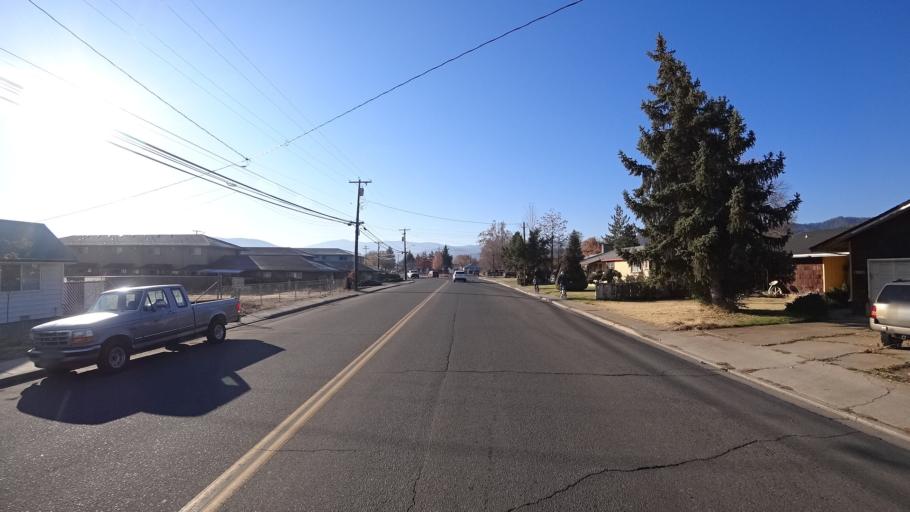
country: US
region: California
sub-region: Siskiyou County
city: Yreka
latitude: 41.7222
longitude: -122.6417
